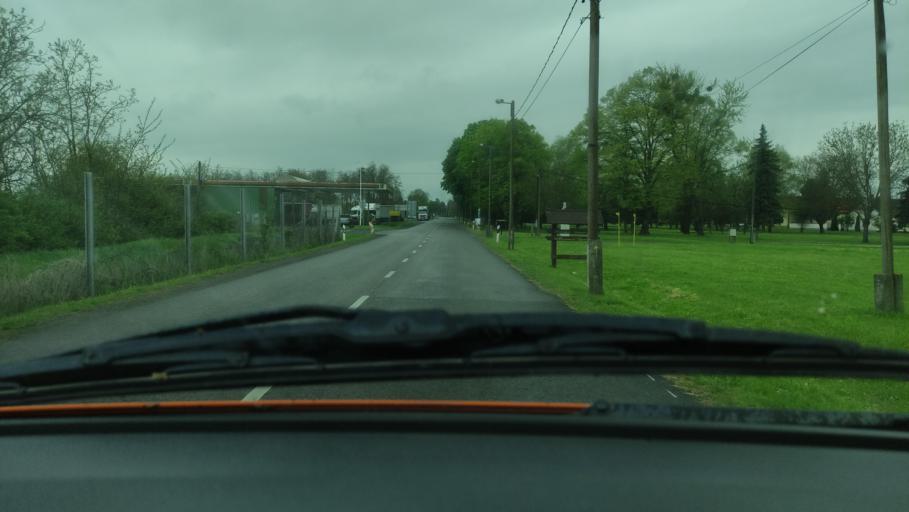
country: HU
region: Baranya
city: Mohacs
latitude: 45.9051
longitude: 18.6598
